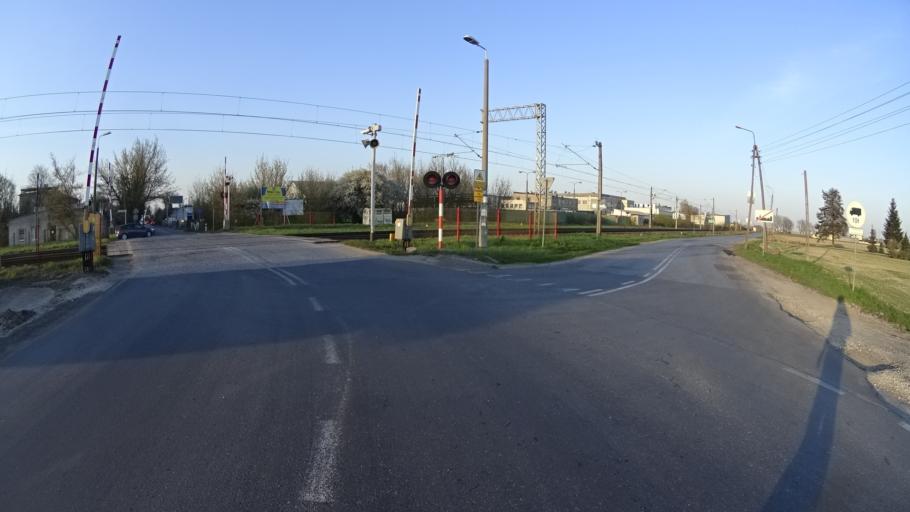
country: PL
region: Masovian Voivodeship
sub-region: Powiat warszawski zachodni
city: Ozarow Mazowiecki
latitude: 52.2069
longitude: 20.8098
